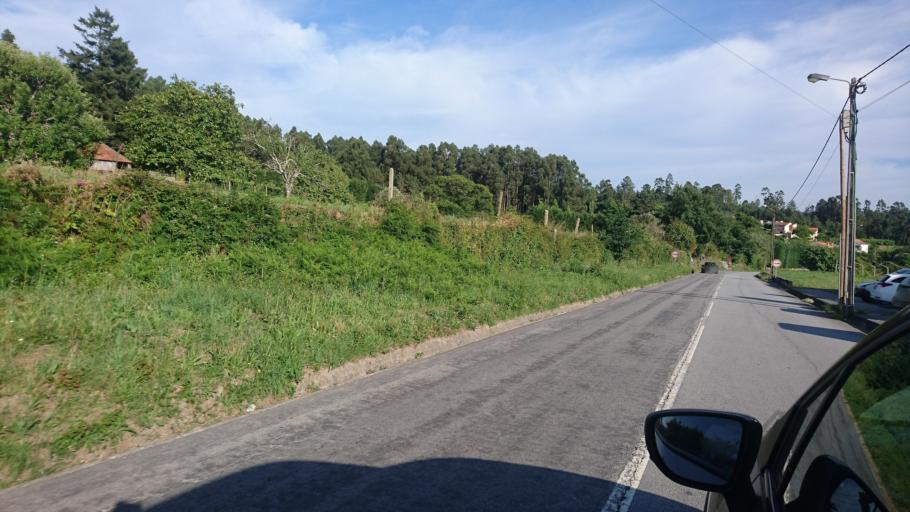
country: PT
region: Porto
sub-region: Paredes
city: Recarei
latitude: 41.1331
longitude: -8.3746
